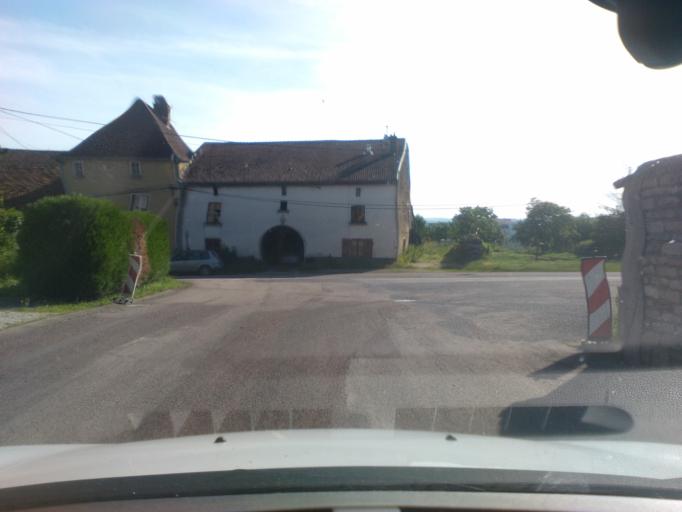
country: FR
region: Lorraine
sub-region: Departement des Vosges
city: Mirecourt
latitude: 48.2486
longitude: 6.2356
